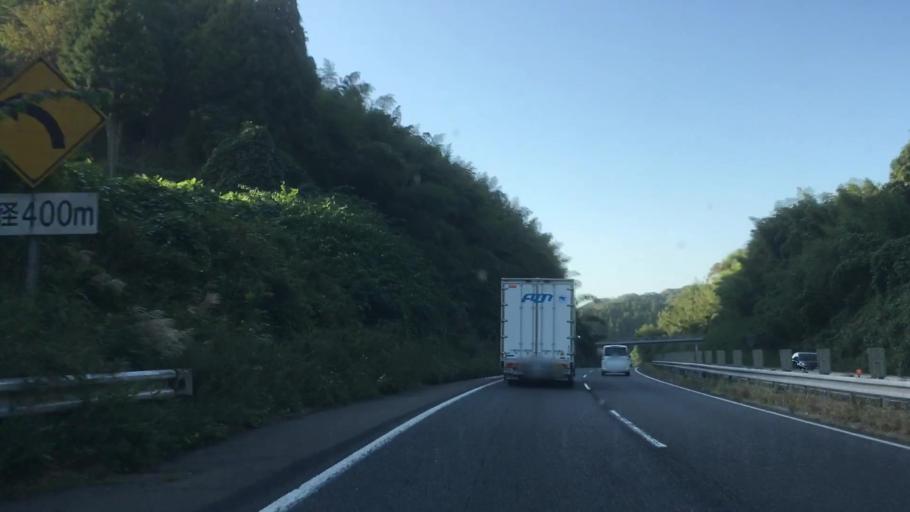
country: JP
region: Yamaguchi
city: Onoda
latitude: 34.1119
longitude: 131.1343
